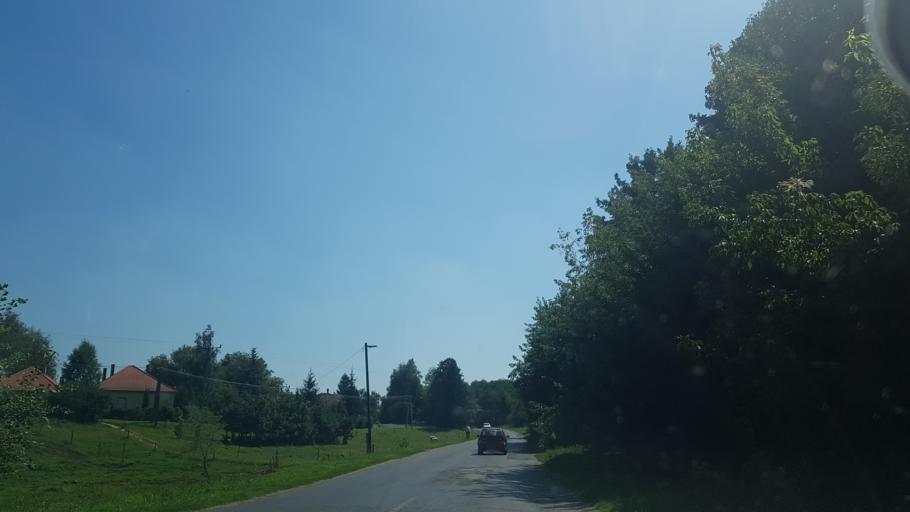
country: HU
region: Somogy
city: Segesd
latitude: 46.2909
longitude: 17.2973
